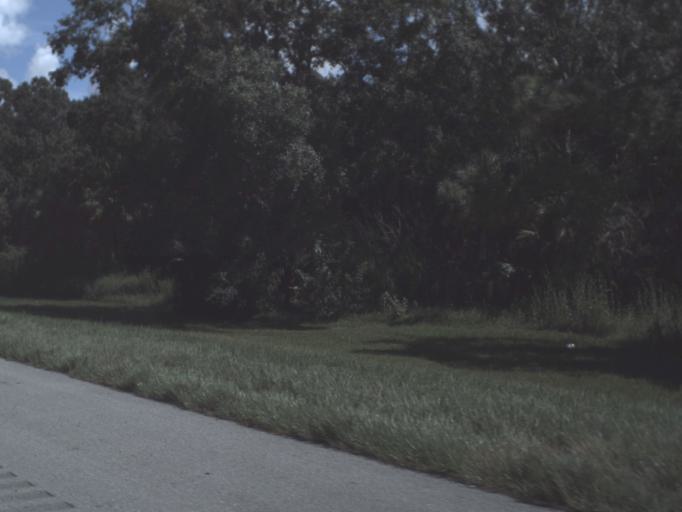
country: US
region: Florida
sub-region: Sarasota County
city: Vamo
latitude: 27.2358
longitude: -82.4519
